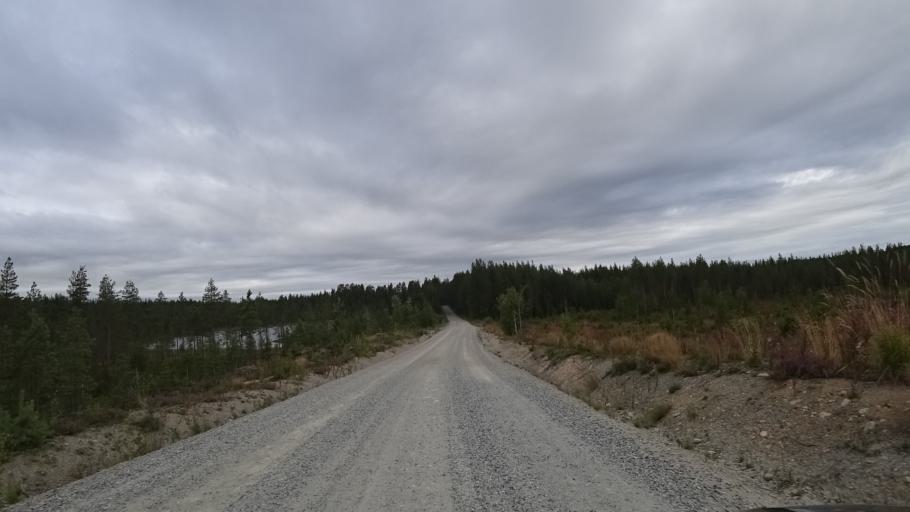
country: FI
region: North Karelia
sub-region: Pielisen Karjala
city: Lieksa
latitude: 63.2527
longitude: 30.3268
